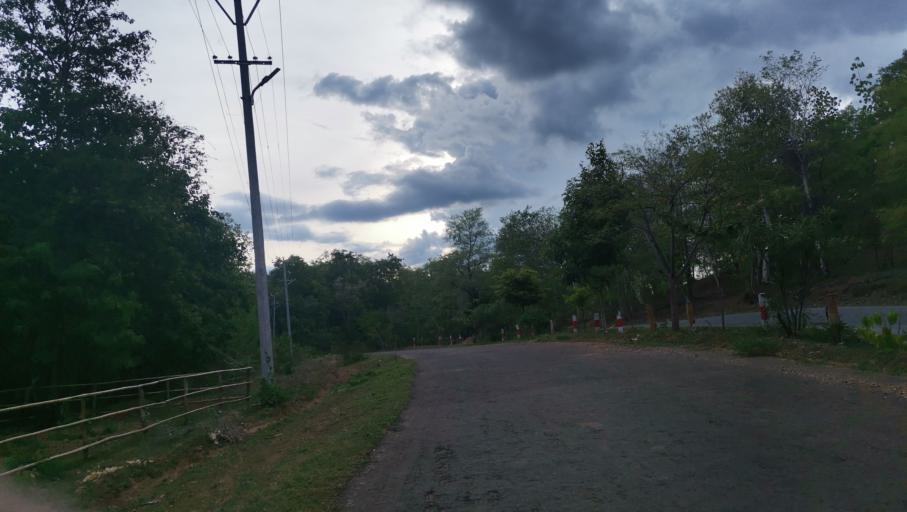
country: MM
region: Magway
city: Minbu
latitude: 20.0885
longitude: 94.5702
